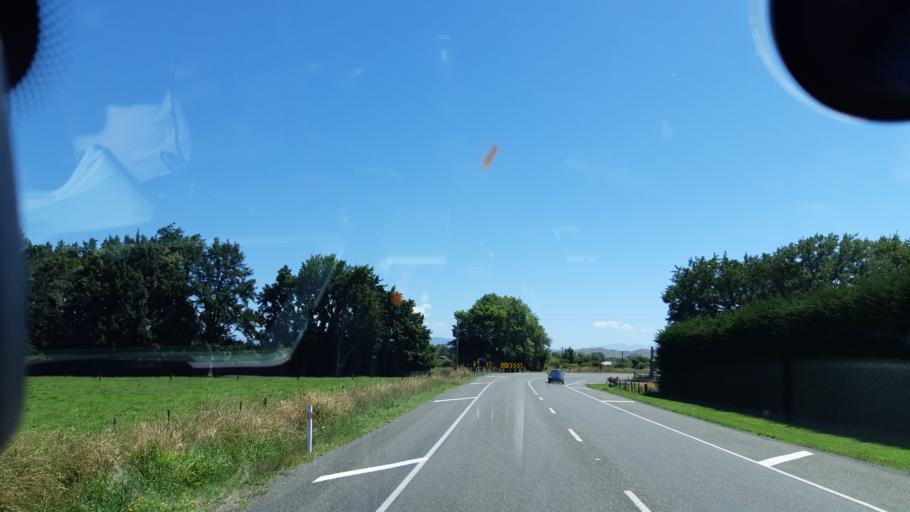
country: NZ
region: Canterbury
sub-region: Kaikoura District
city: Kaikoura
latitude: -42.7407
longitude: 173.2666
